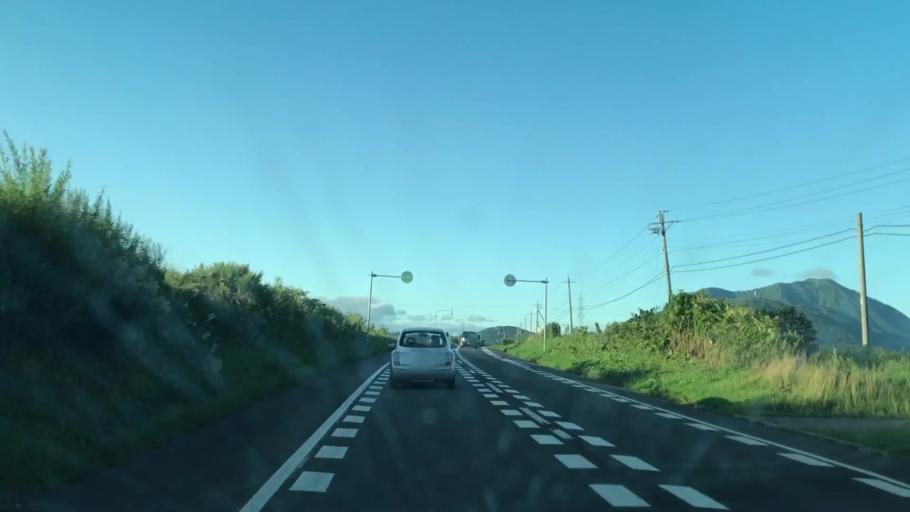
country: JP
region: Hokkaido
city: Niseko Town
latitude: 42.7164
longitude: 140.8591
